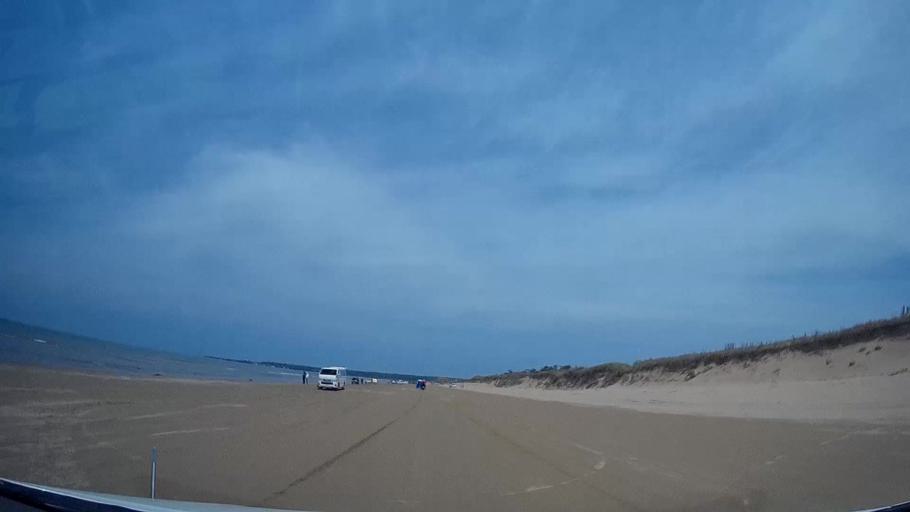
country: JP
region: Ishikawa
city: Hakui
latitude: 36.8820
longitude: 136.7629
